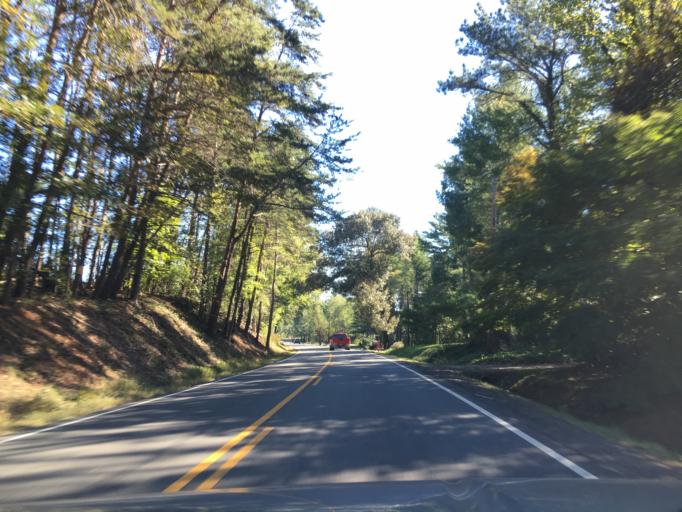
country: US
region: Virginia
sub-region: Goochland County
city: Goochland
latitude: 37.6969
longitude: -77.8685
